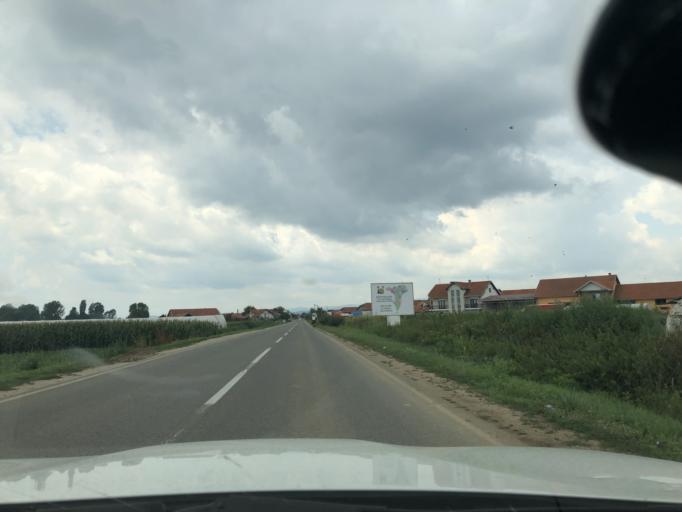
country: RS
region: Central Serbia
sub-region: Jablanicki Okrug
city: Leskovac
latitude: 42.9654
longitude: 21.8503
